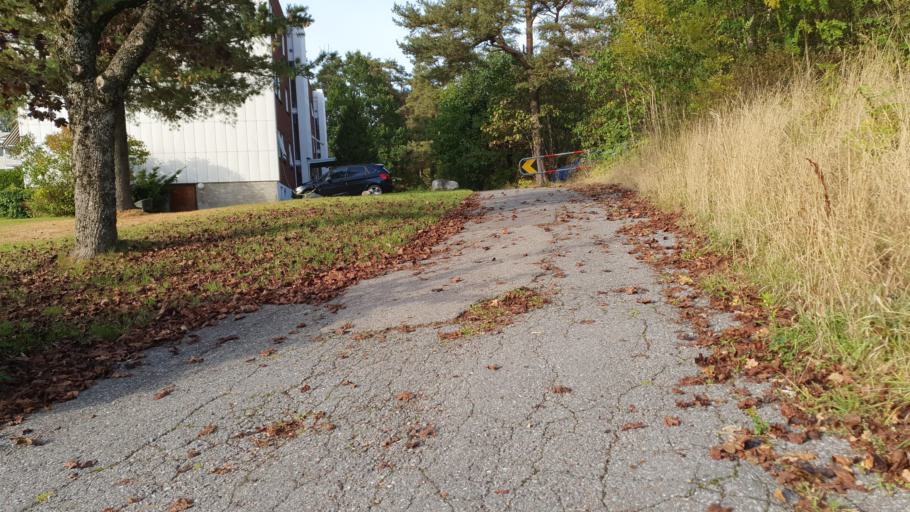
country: NO
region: Vestfold
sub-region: Tonsberg
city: Tonsberg
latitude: 59.2801
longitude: 10.4261
